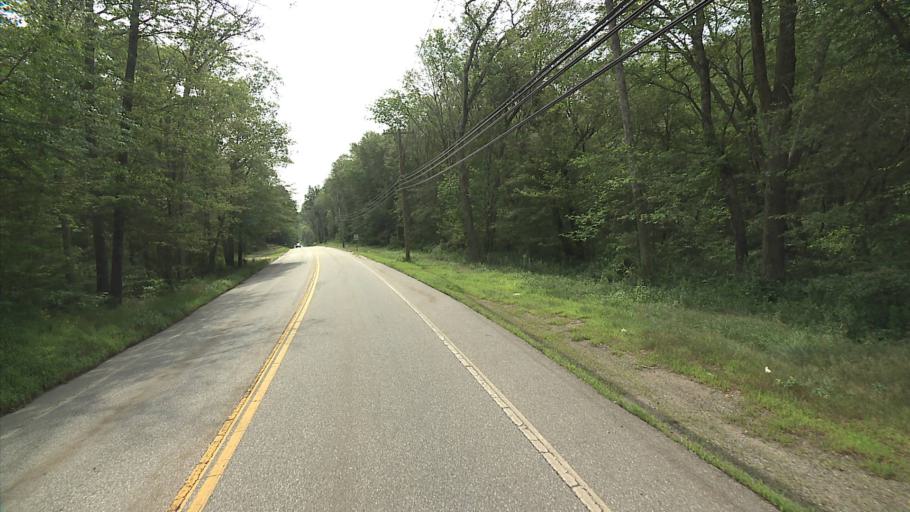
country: US
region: Connecticut
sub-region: Windham County
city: Danielson
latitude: 41.8056
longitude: -71.8619
